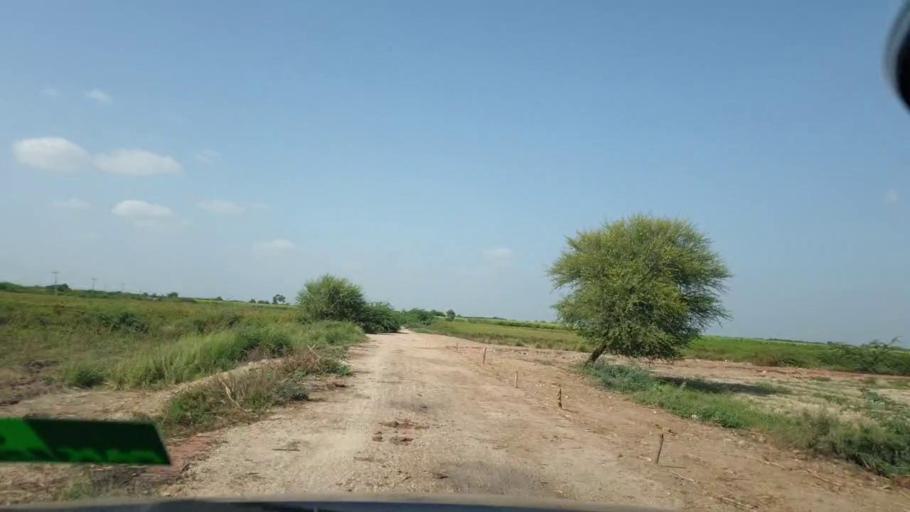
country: PK
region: Sindh
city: Tando Bago
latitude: 24.6860
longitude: 69.2056
